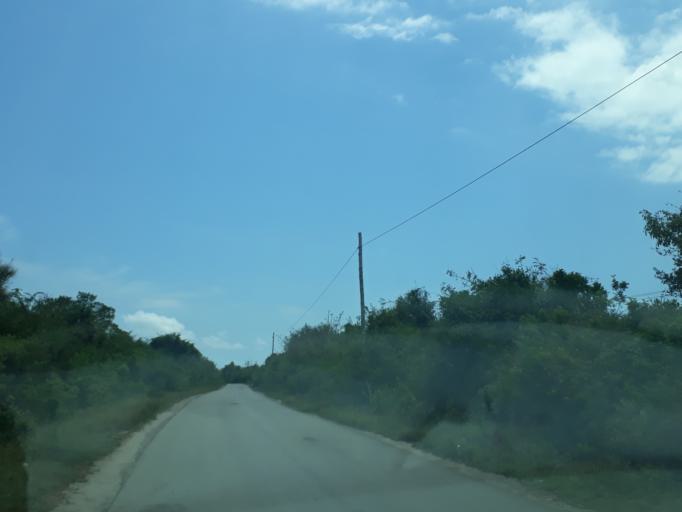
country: TZ
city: Kiwengwa
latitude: -5.9921
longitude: 39.3649
